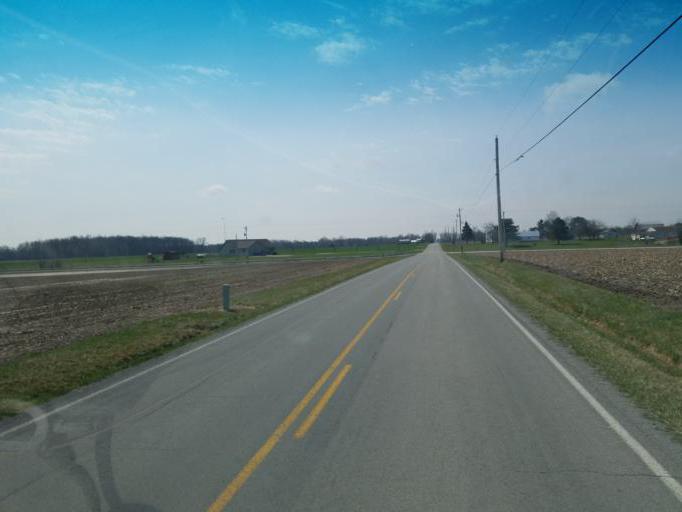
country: US
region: Ohio
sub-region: Wyandot County
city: Upper Sandusky
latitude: 40.8928
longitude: -83.1701
